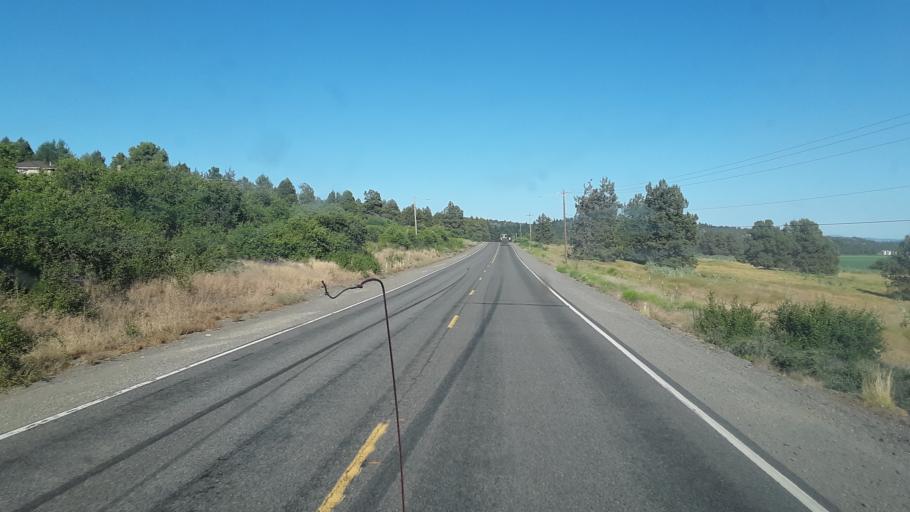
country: US
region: Oregon
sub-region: Klamath County
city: Klamath Falls
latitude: 42.2756
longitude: -121.9026
